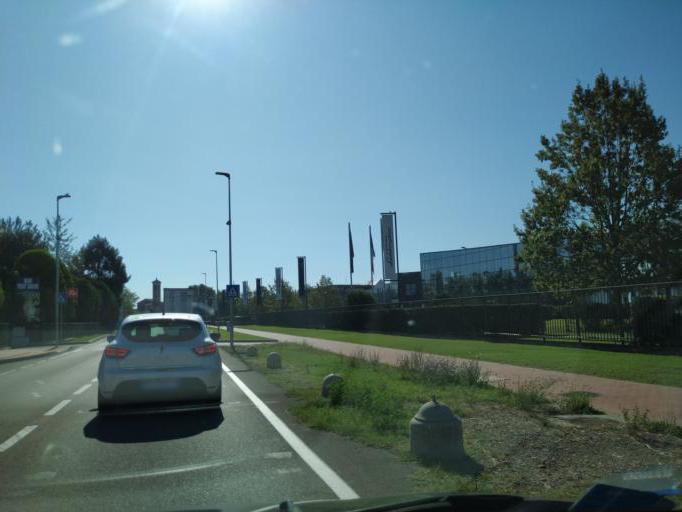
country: IT
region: Emilia-Romagna
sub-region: Provincia di Bologna
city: Sant'Agata Bolognese
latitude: 44.6599
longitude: 11.1252
